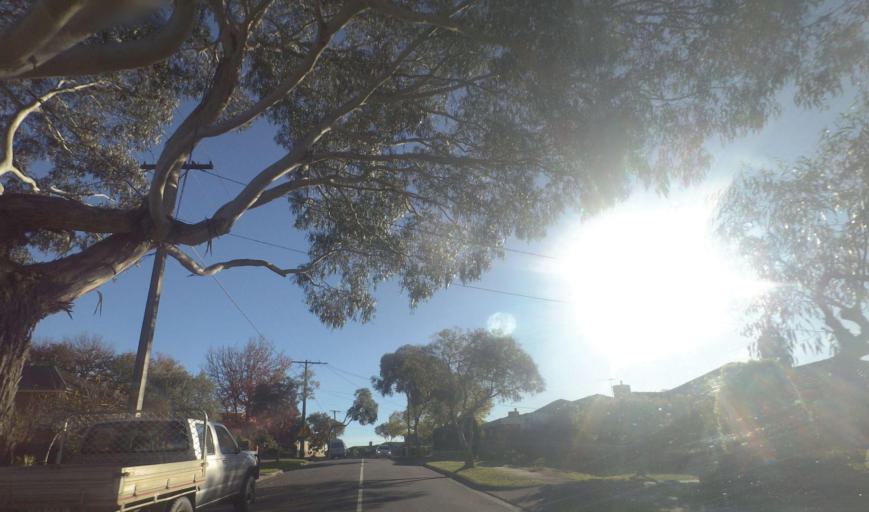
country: AU
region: Victoria
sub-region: Whitehorse
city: Blackburn North
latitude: -37.8071
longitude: 145.1465
